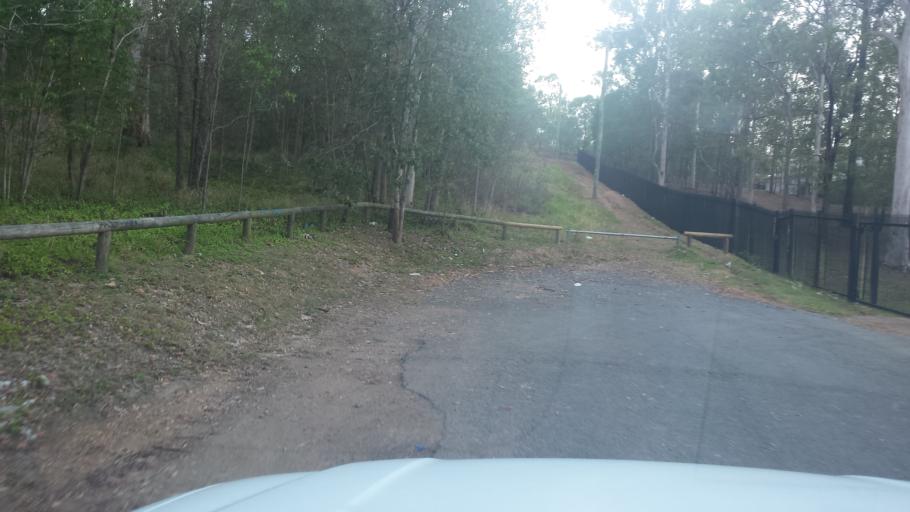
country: AU
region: Queensland
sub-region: Logan
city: Logan City
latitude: -27.6642
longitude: 153.1095
